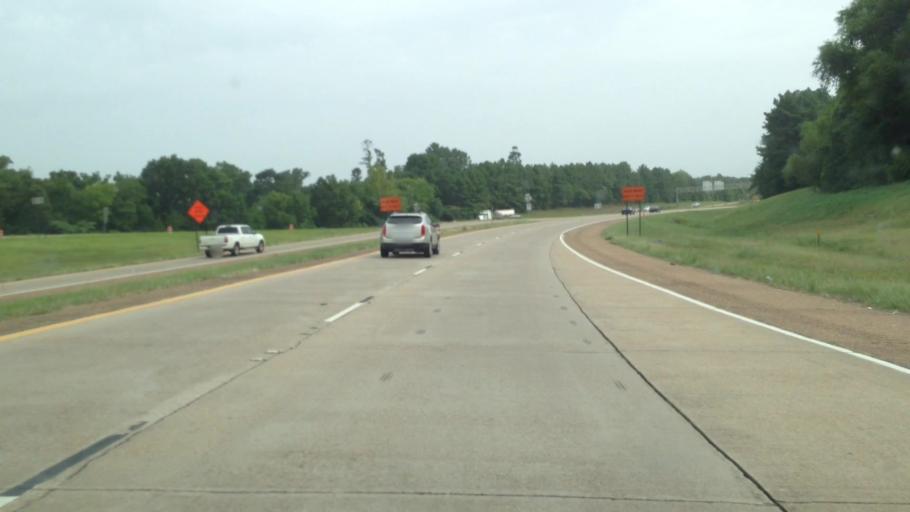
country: US
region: Louisiana
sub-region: Caddo Parish
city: Shreveport
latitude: 32.4605
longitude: -93.8456
